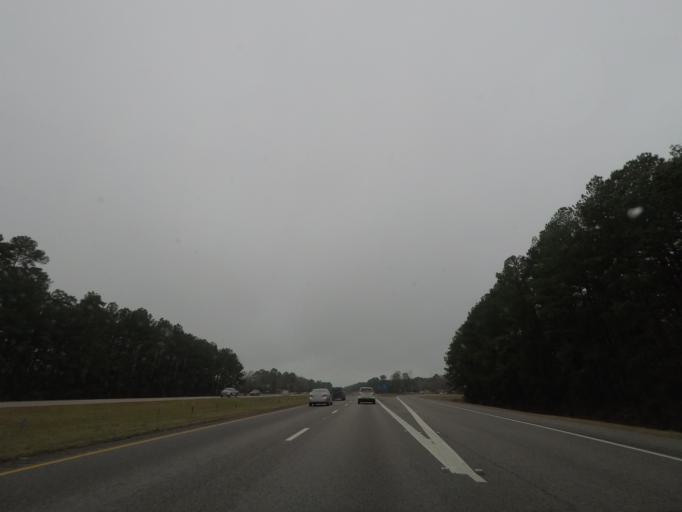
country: US
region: South Carolina
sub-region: Florence County
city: Timmonsville
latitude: 33.9508
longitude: -80.0543
